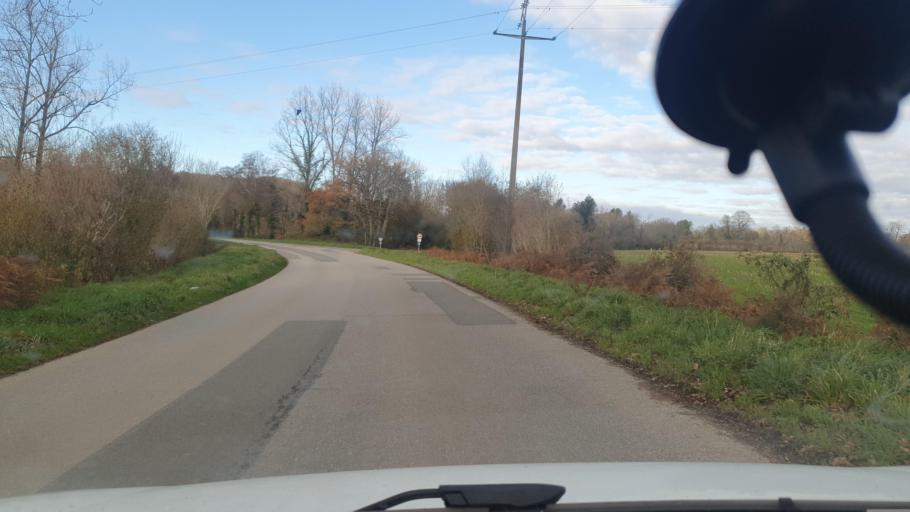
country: FR
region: Brittany
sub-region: Departement du Finistere
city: Edern
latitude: 48.0872
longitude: -3.9904
